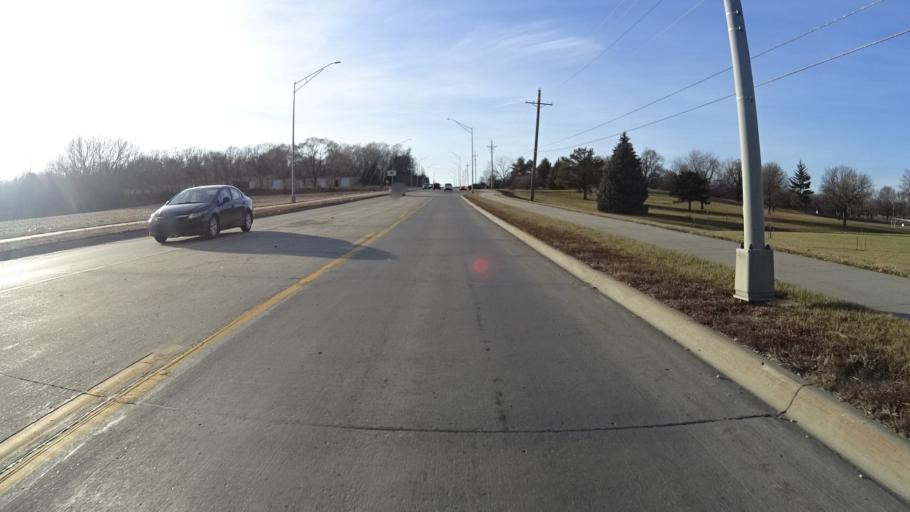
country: US
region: Nebraska
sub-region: Sarpy County
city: La Vista
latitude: 41.1908
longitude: -96.0153
